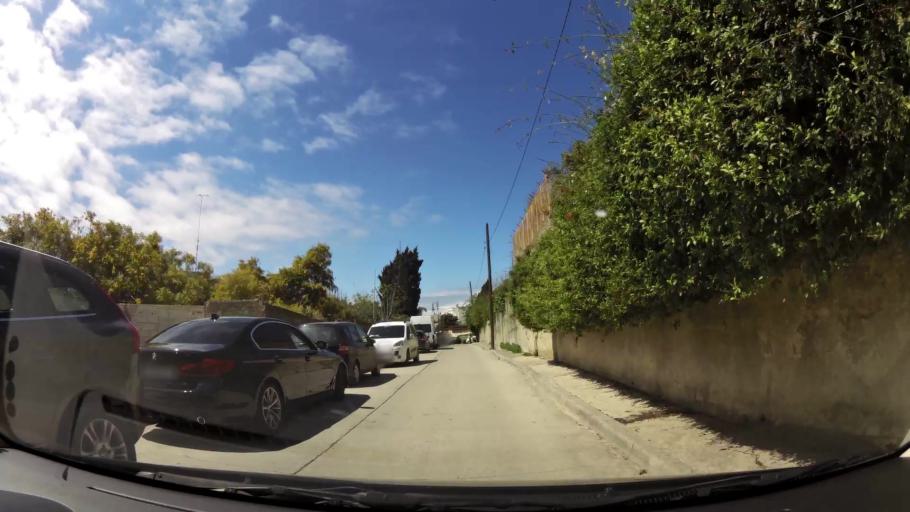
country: MA
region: Tanger-Tetouan
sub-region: Tanger-Assilah
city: Tangier
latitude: 35.7794
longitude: -5.8281
